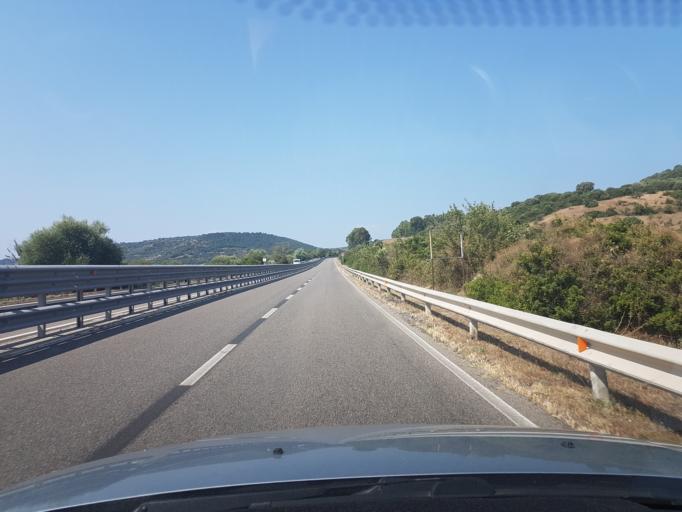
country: IT
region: Sardinia
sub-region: Provincia di Oristano
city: Sedilo
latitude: 40.1514
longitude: 8.8997
